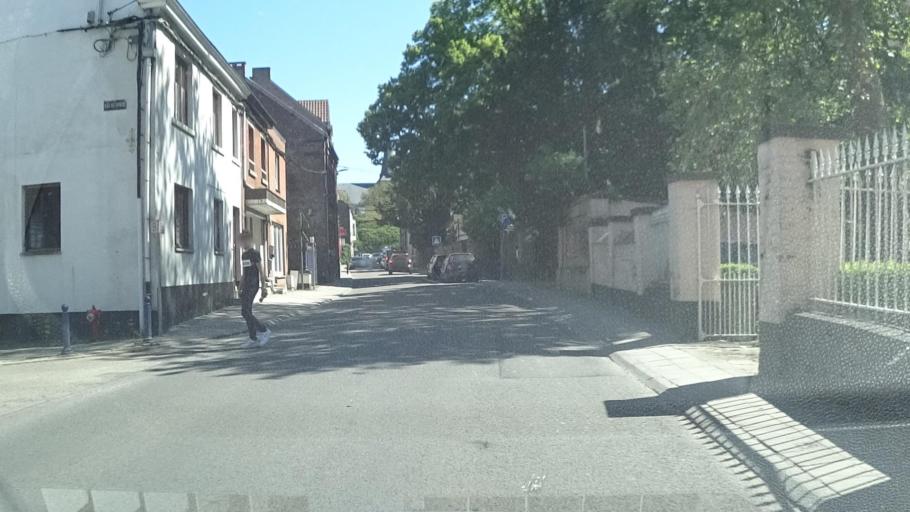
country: BE
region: Wallonia
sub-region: Province du Brabant Wallon
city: Court-Saint-Etienne
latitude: 50.6449
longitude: 4.5670
